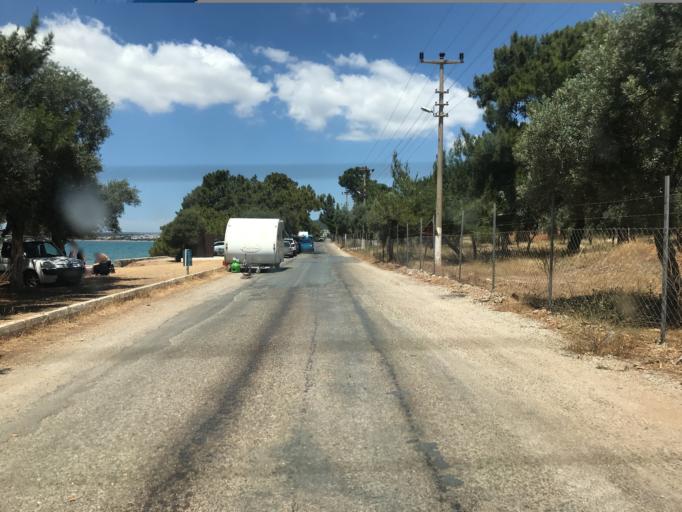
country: TR
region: Aydin
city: Sarikemer
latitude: 37.4067
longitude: 27.4263
